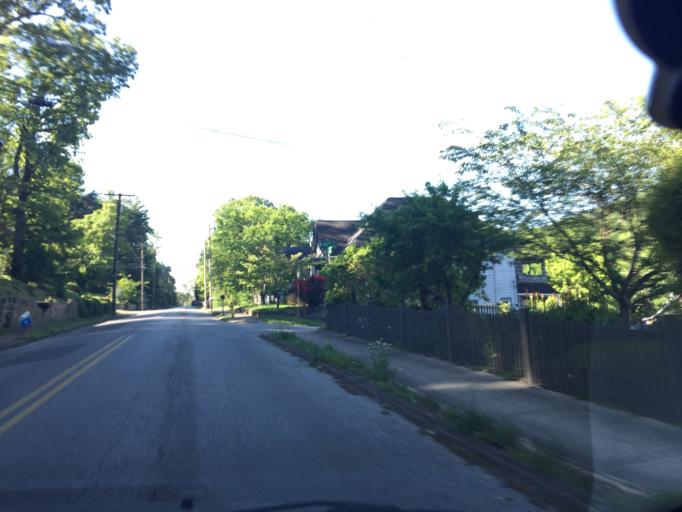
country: US
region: Tennessee
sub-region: Hamilton County
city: Lookout Mountain
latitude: 35.0036
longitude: -85.3276
